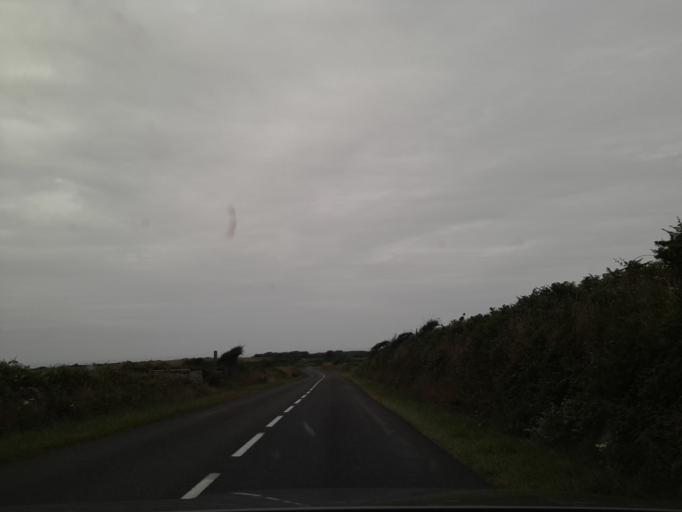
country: FR
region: Lower Normandy
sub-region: Departement de la Manche
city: Beaumont-Hague
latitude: 49.7015
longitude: -1.9281
